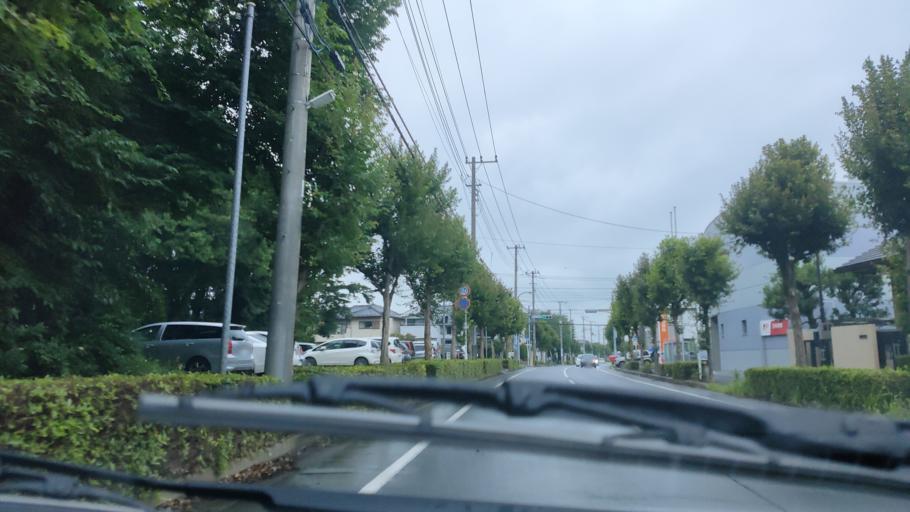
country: JP
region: Chiba
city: Nagareyama
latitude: 35.8776
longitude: 139.9162
